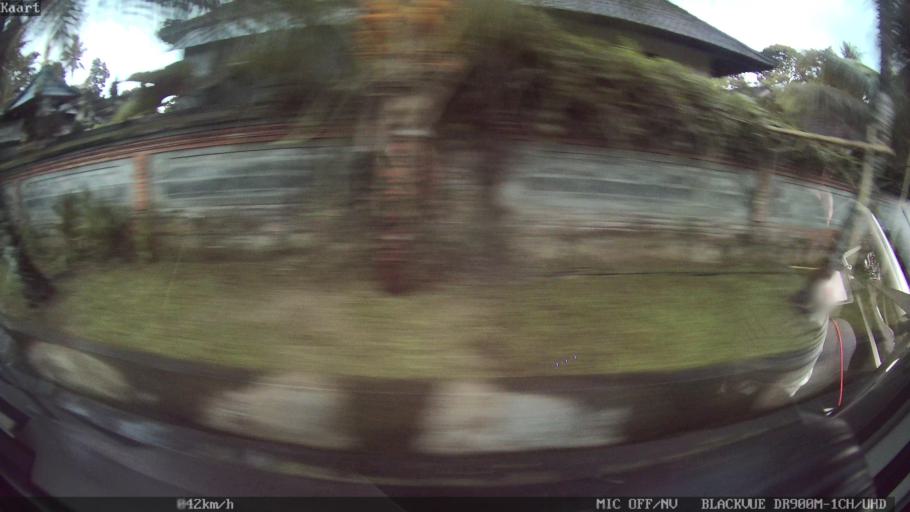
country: ID
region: Bali
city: Banjar Teguan
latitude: -8.5005
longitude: 115.2366
